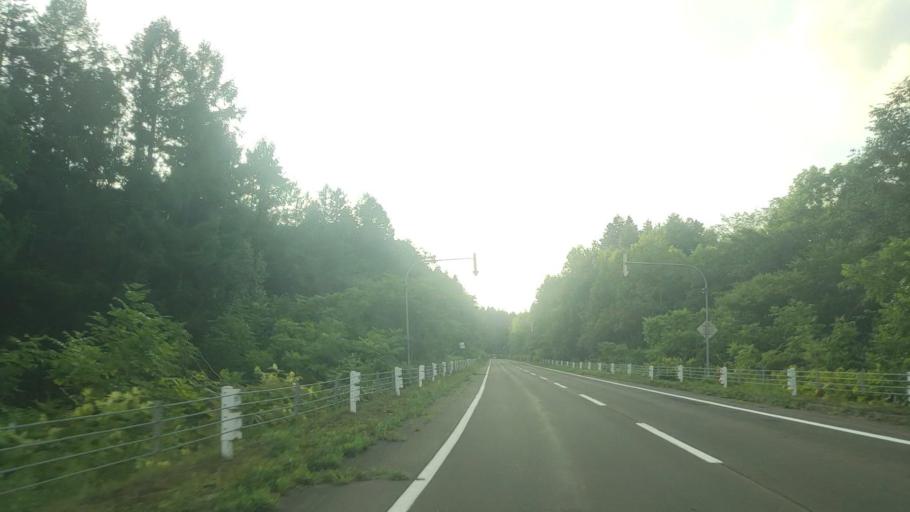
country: JP
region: Hokkaido
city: Bibai
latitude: 43.1398
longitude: 142.0961
